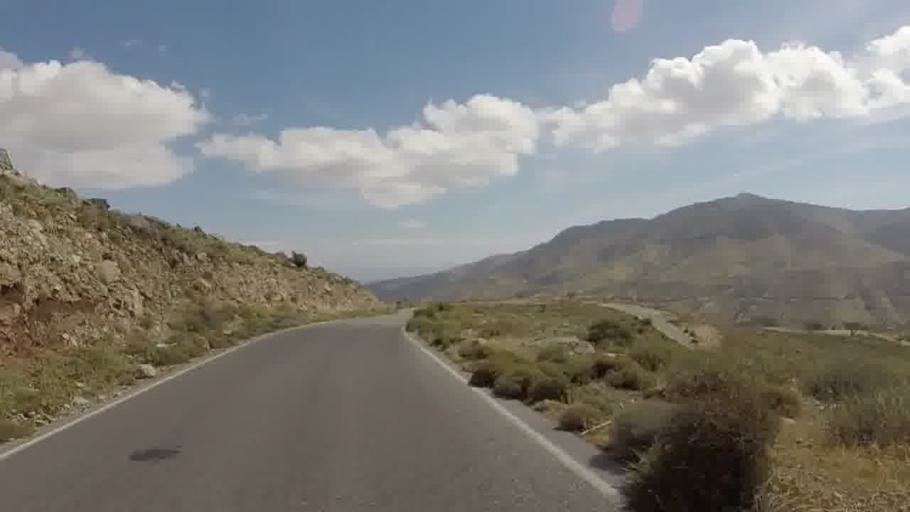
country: GR
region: Crete
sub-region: Nomos Rethymnis
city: Agia Galini
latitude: 35.1547
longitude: 24.6211
